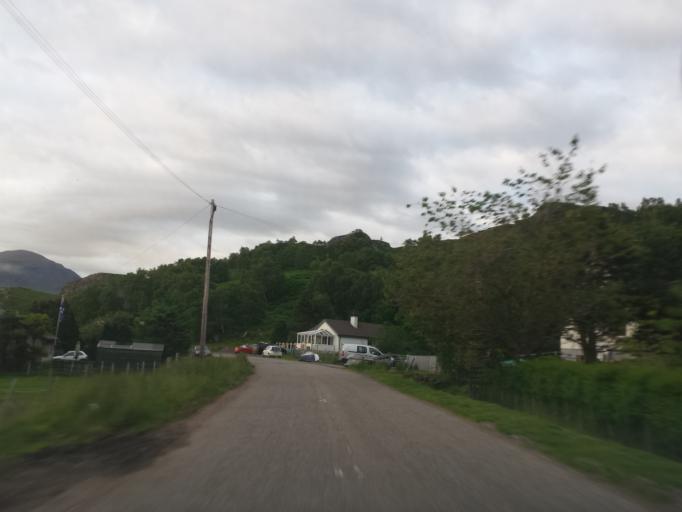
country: GB
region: Scotland
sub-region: Highland
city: Portree
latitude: 57.5204
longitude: -5.6466
